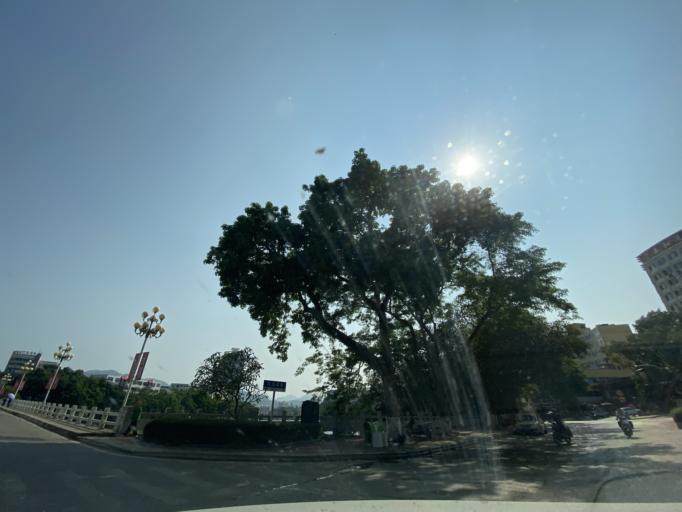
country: CN
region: Hainan
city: Chongshan
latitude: 18.7823
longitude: 109.5113
